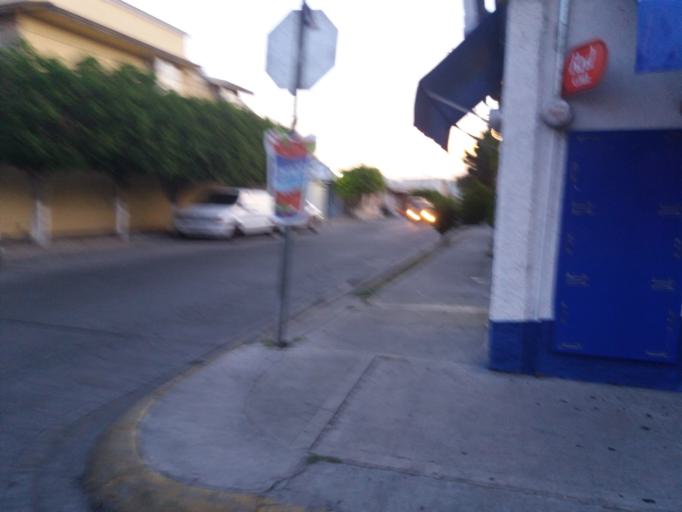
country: MX
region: Aguascalientes
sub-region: Aguascalientes
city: Aguascalientes
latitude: 21.8617
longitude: -102.2712
